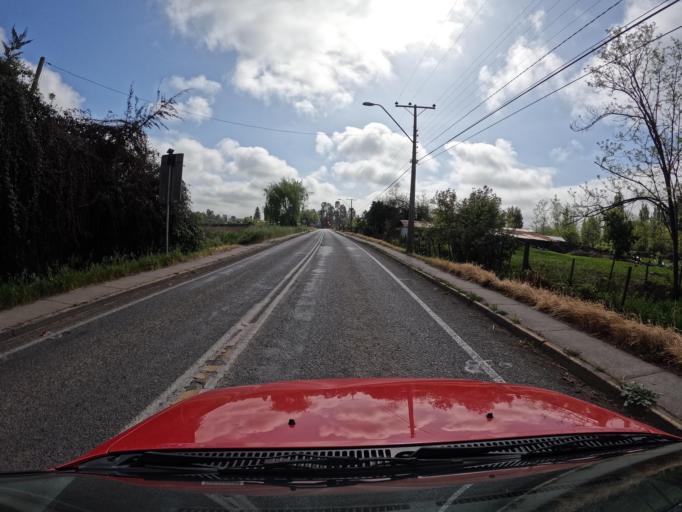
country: CL
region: Maule
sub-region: Provincia de Curico
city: Teno
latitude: -34.8619
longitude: -71.1967
